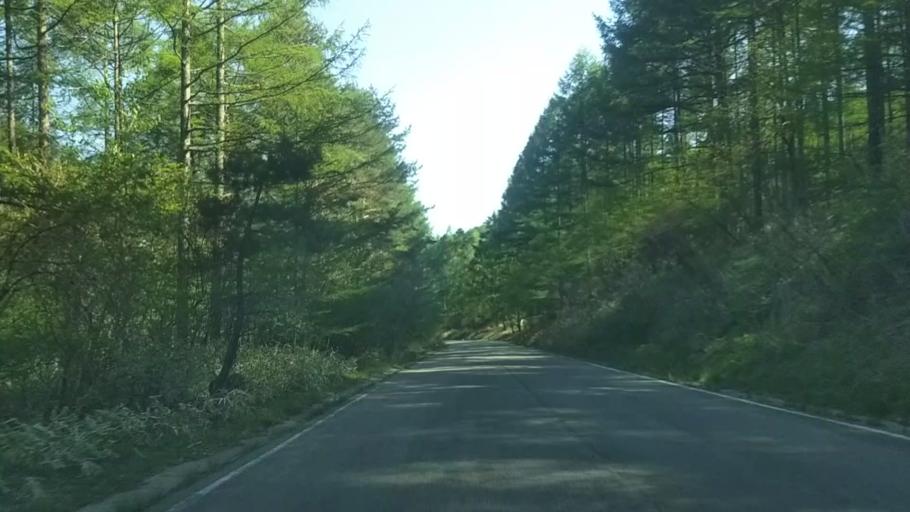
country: JP
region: Yamanashi
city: Nirasaki
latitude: 35.9206
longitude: 138.4026
